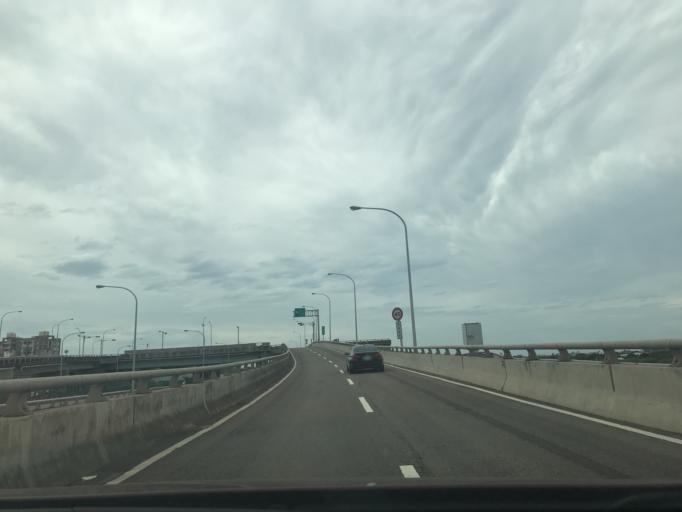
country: TW
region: Taiwan
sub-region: Hsinchu
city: Hsinchu
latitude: 24.8258
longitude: 120.9736
